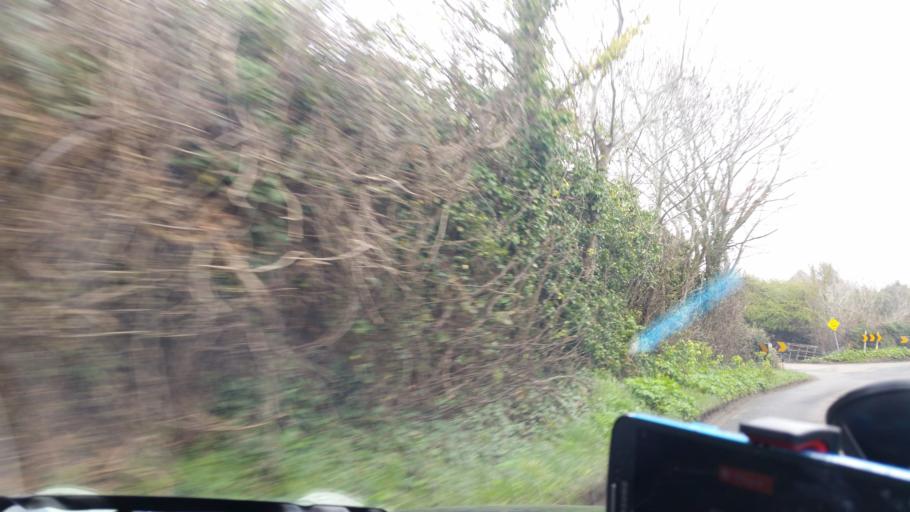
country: IE
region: Leinster
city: Portmarnock
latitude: 53.4276
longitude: -6.1545
